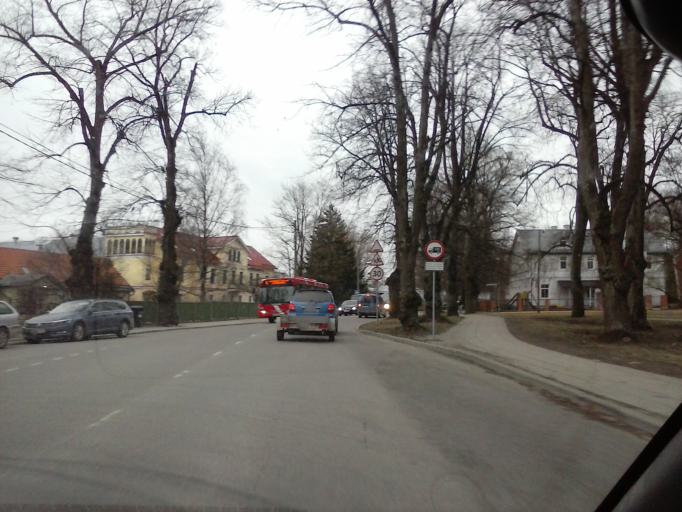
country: EE
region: Tartu
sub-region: Tartu linn
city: Tartu
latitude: 58.3838
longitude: 26.7086
